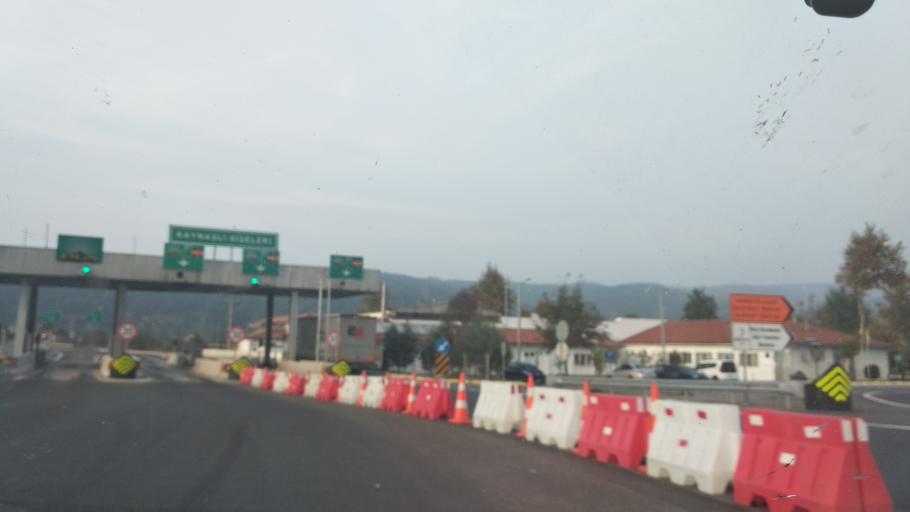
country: TR
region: Duzce
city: Kaynasli
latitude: 40.7835
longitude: 31.2781
